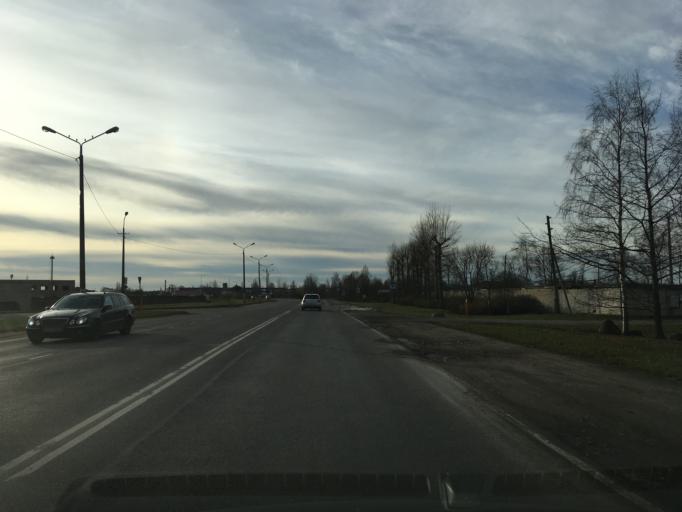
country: EE
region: Ida-Virumaa
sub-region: Narva linn
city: Narva
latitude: 59.3798
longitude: 28.1560
